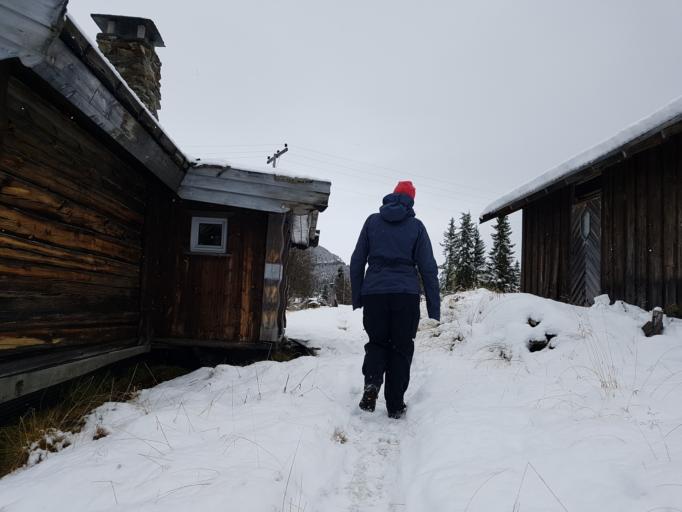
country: NO
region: Oppland
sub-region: Sel
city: Otta
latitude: 61.8078
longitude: 9.6802
